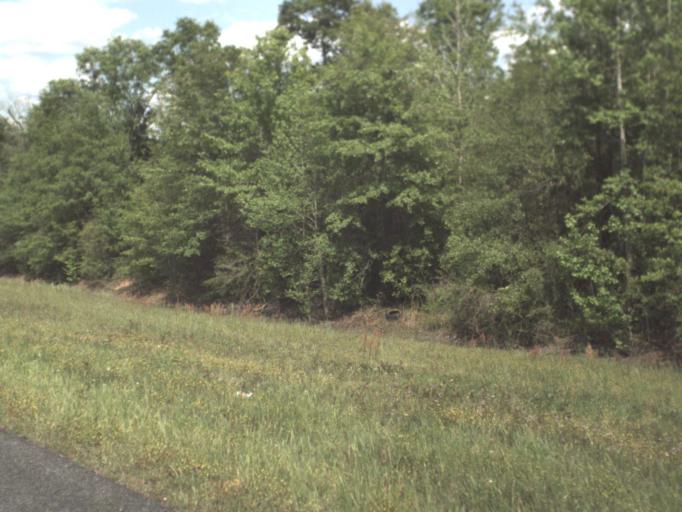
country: US
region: Florida
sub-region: Escambia County
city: Molino
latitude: 30.7719
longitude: -87.3398
